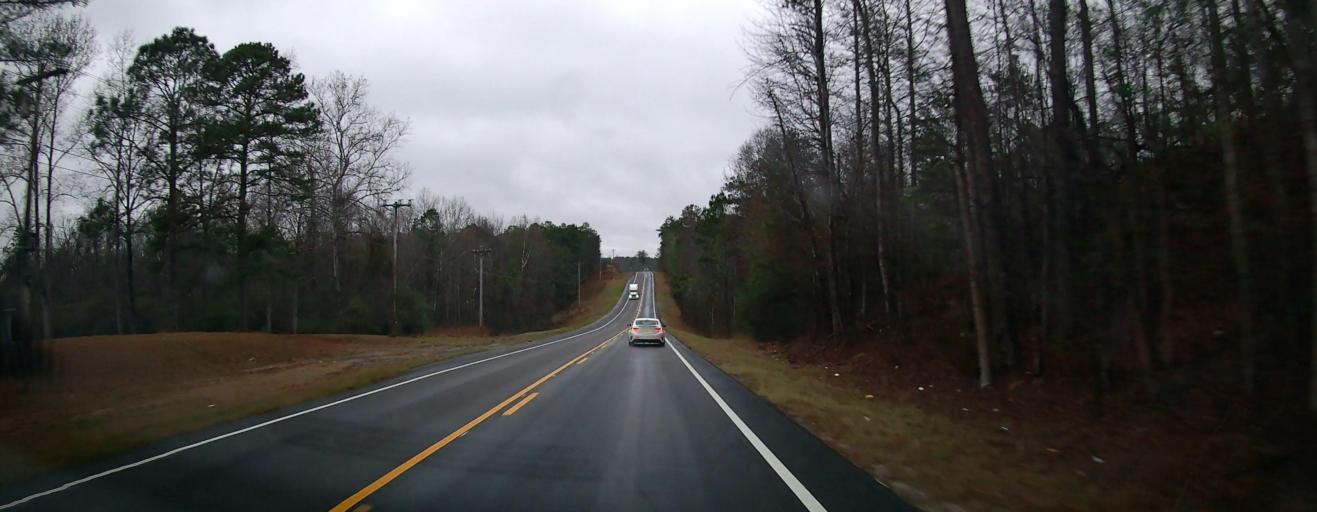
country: US
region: Alabama
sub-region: Chilton County
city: Clanton
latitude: 32.6931
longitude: -86.7977
